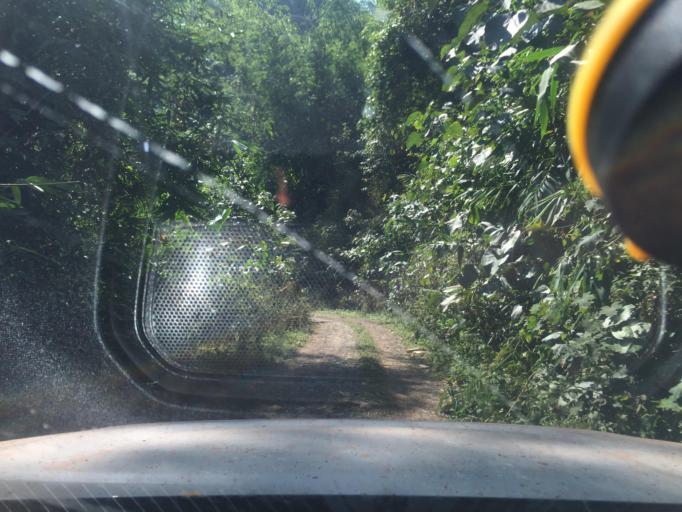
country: LA
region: Phongsali
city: Phongsali
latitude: 21.7045
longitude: 102.3966
